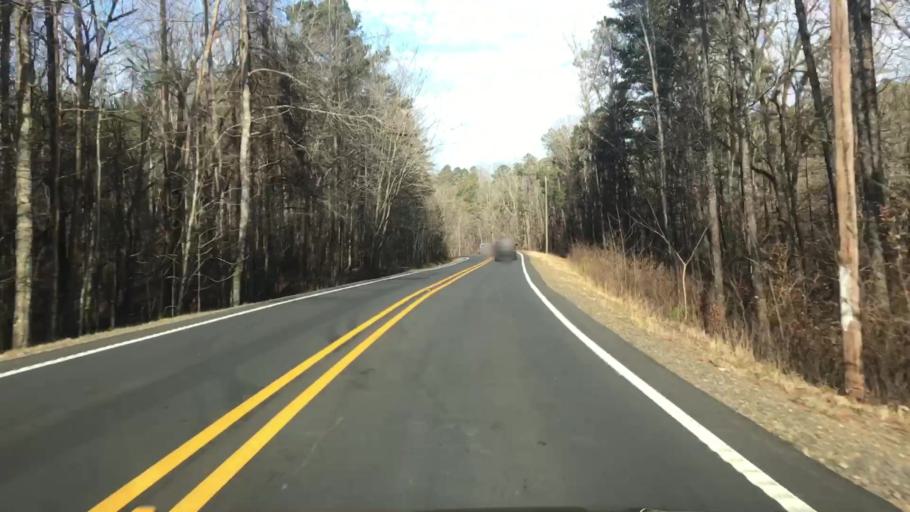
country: US
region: Arkansas
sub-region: Montgomery County
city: Mount Ida
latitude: 34.5233
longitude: -93.3998
